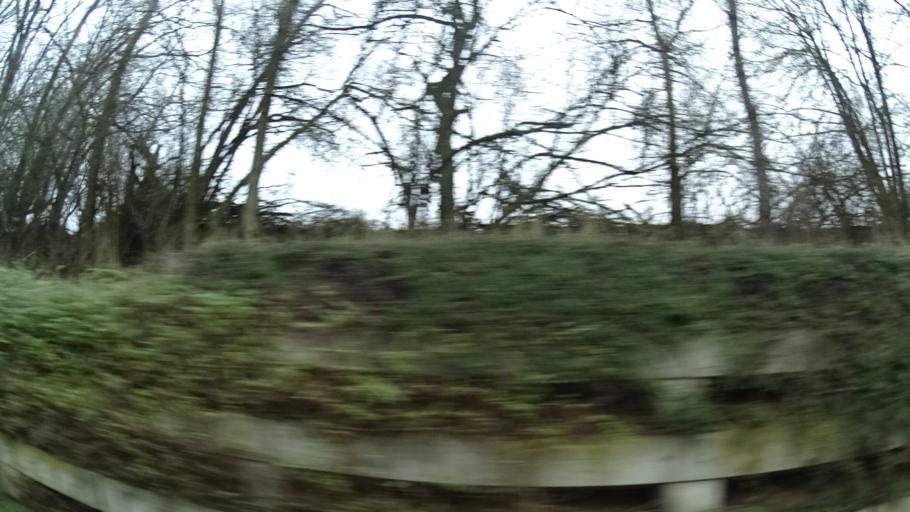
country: DE
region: Baden-Wuerttemberg
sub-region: Karlsruhe Region
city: Osterburken
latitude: 49.4695
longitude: 9.4158
